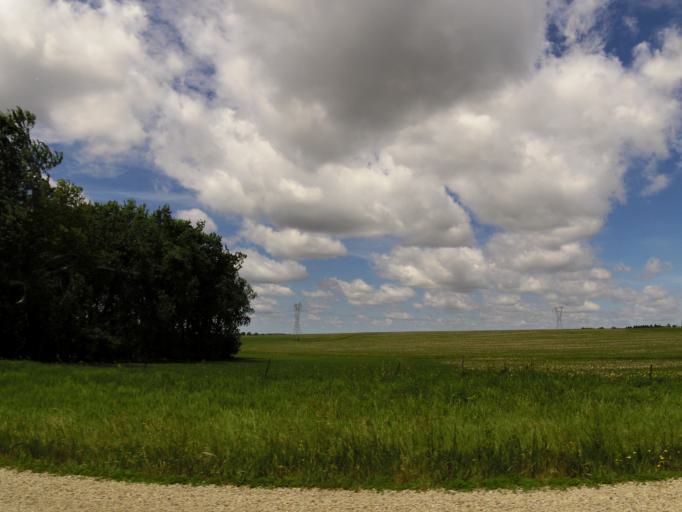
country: US
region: Iowa
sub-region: Chickasaw County
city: New Hampton
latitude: 43.1160
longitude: -92.2979
